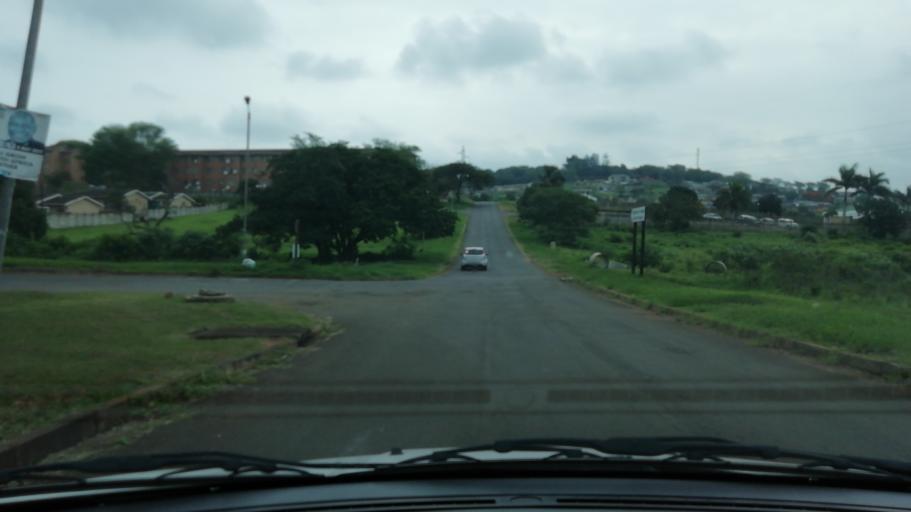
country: ZA
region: KwaZulu-Natal
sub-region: uThungulu District Municipality
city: Empangeni
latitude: -28.7387
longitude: 31.8861
